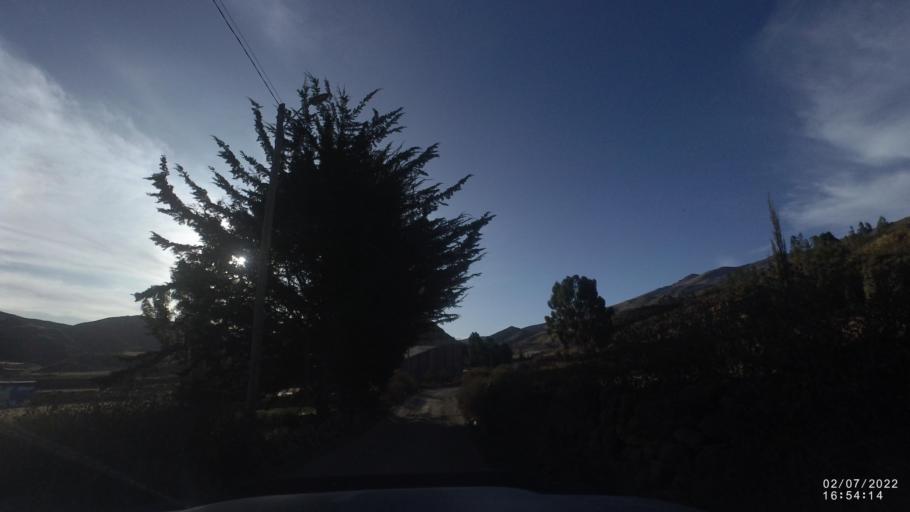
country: BO
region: Cochabamba
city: Irpa Irpa
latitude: -17.9666
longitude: -66.5390
